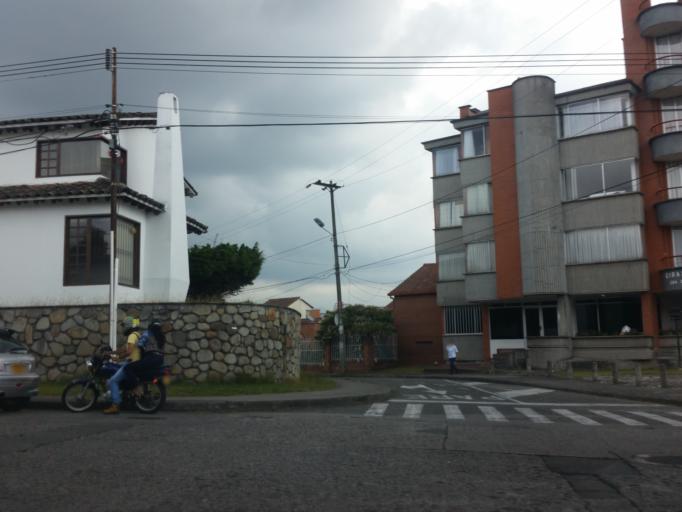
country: CO
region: Caldas
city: Manizales
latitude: 5.0598
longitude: -75.4970
